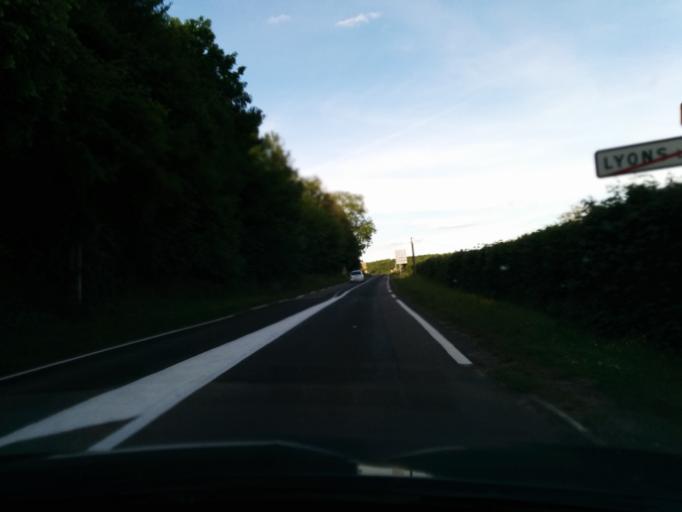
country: FR
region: Haute-Normandie
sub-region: Departement de la Seine-Maritime
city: La Feuillie
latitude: 49.4036
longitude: 1.4783
